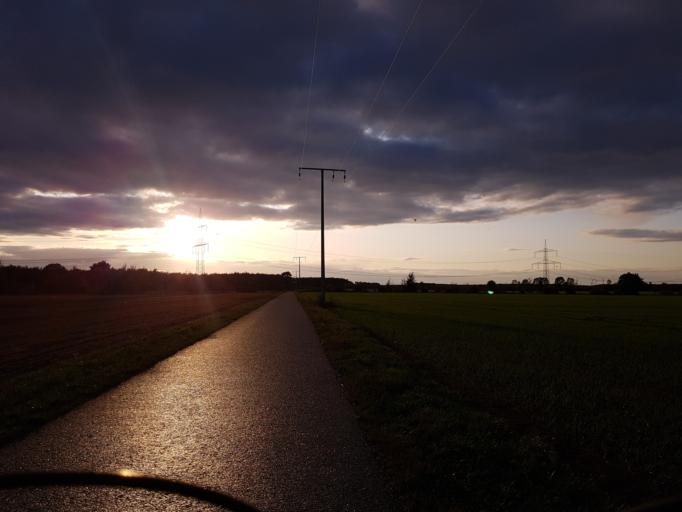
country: DE
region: Brandenburg
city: Bad Liebenwerda
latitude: 51.5454
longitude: 13.4138
